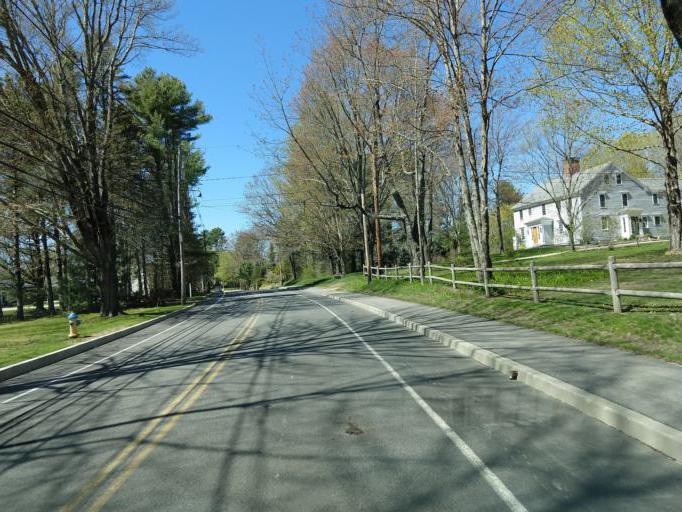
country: US
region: Maine
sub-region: York County
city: Kennebunkport
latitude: 43.3709
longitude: -70.4731
